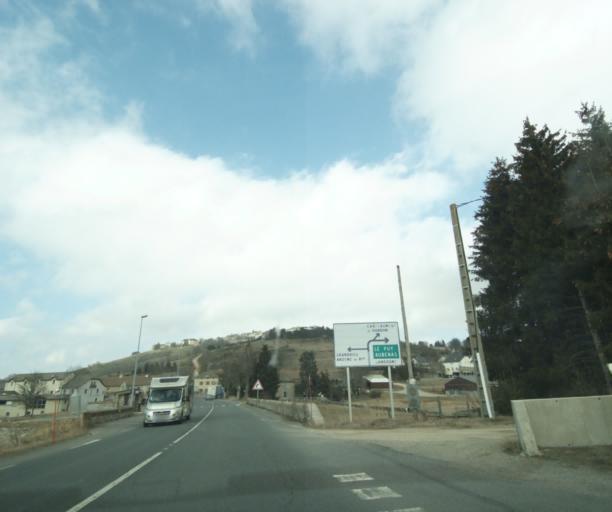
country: FR
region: Languedoc-Roussillon
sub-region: Departement de la Lozere
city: Langogne
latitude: 44.6327
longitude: 3.6762
